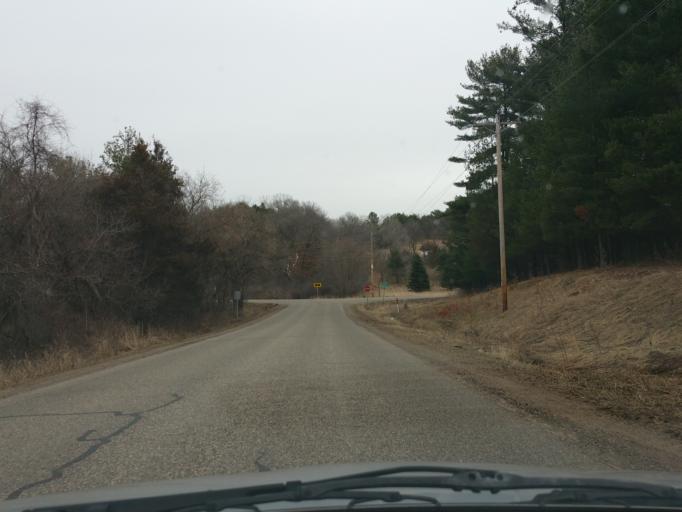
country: US
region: Wisconsin
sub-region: Saint Croix County
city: Roberts
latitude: 45.0034
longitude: -92.6309
